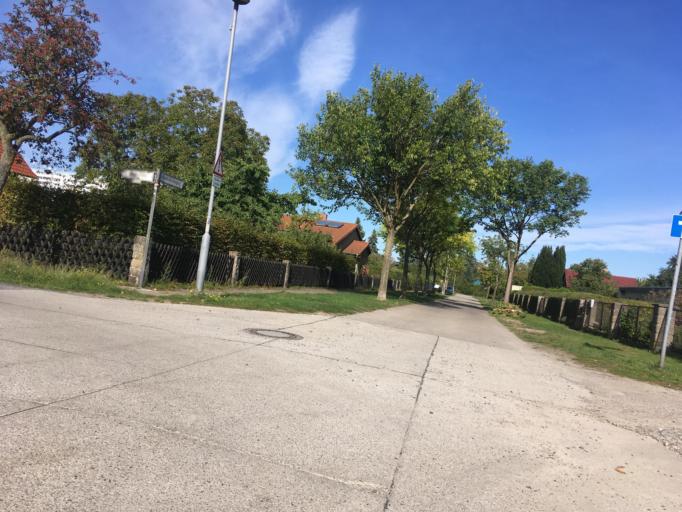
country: DE
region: Berlin
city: Altglienicke
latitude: 52.4021
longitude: 13.5313
